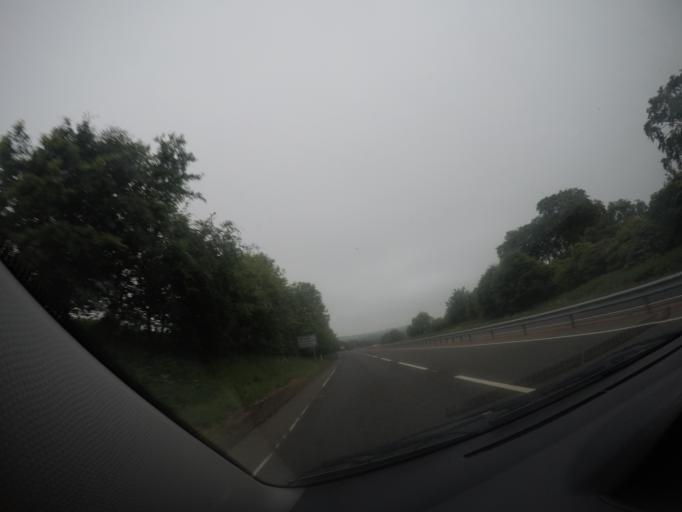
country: GB
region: Scotland
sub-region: Angus
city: Forfar
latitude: 56.5831
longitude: -2.9131
